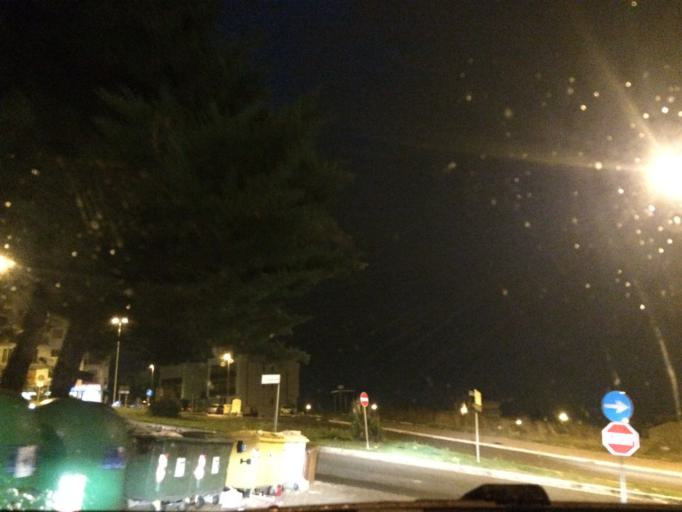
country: IT
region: Basilicate
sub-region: Provincia di Matera
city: Matera
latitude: 40.6719
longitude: 16.5906
